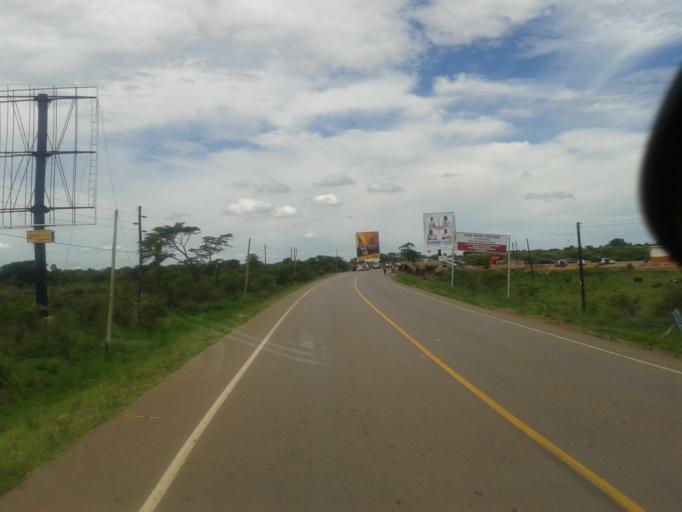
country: UG
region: Western Region
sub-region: Kiryandongo District
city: Masindi Port
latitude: 1.5468
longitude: 32.0409
